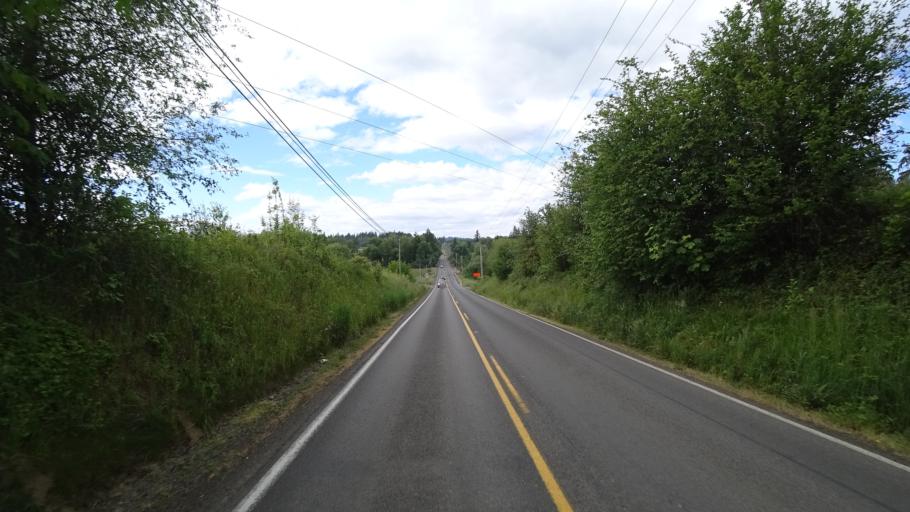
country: US
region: Oregon
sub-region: Washington County
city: Bethany
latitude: 45.5659
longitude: -122.8676
